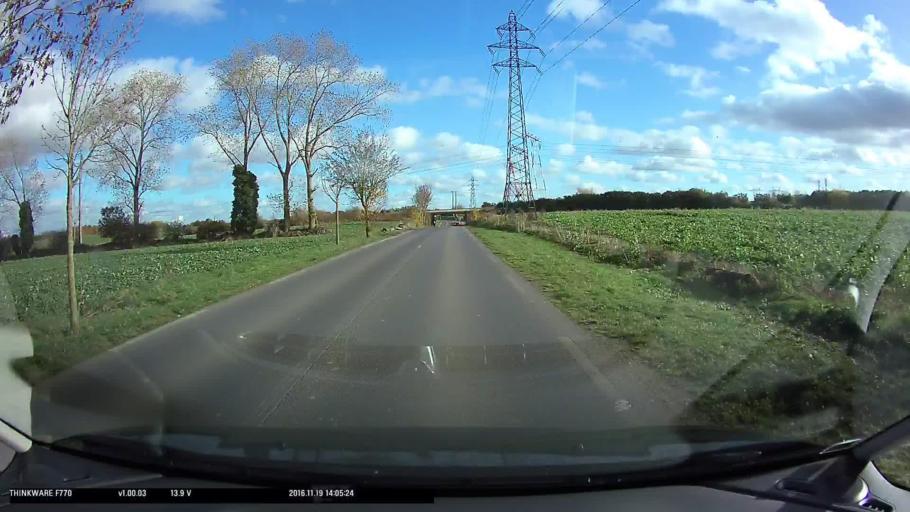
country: FR
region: Ile-de-France
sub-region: Departement du Val-d'Oise
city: Courdimanche
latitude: 49.0596
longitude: 2.0086
